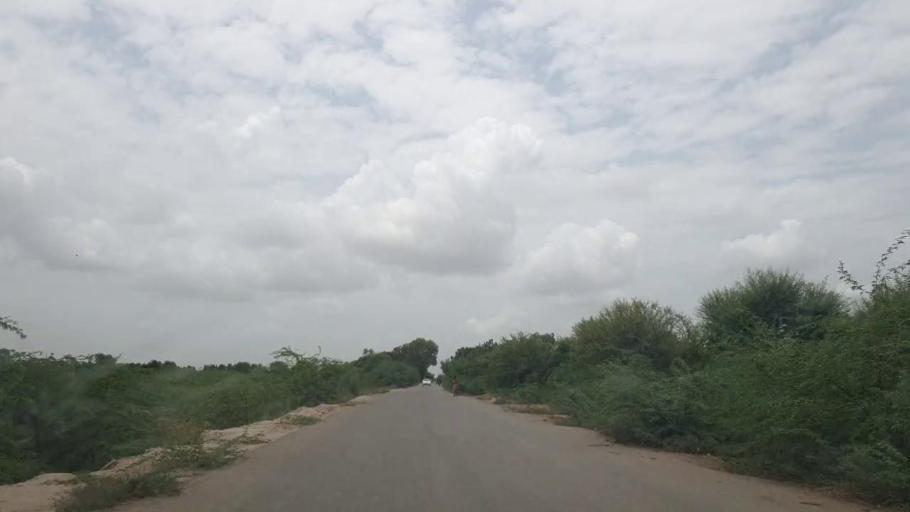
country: PK
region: Sindh
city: Naukot
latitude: 24.9341
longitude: 69.2775
